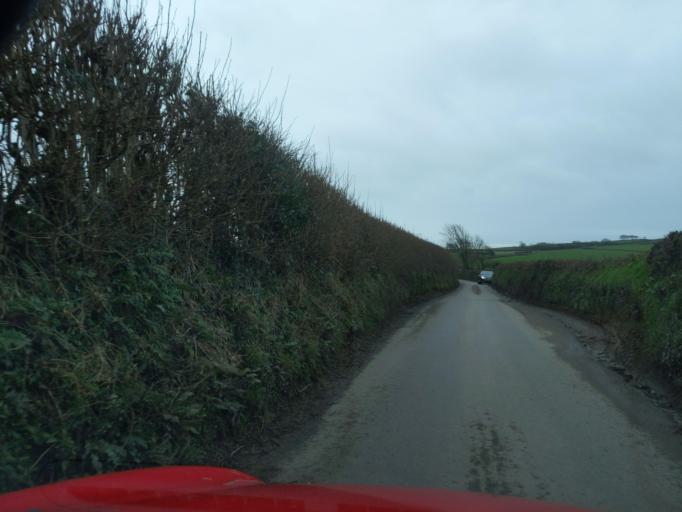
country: GB
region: England
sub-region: Devon
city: Modbury
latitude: 50.3370
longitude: -3.8680
